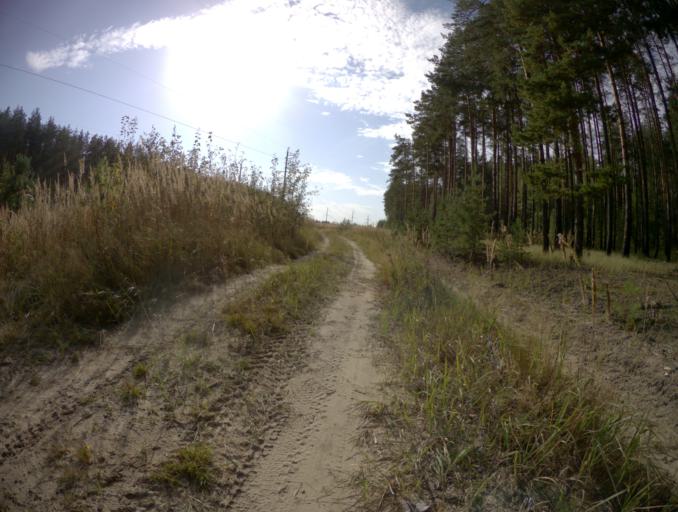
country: RU
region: Vladimir
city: Raduzhnyy
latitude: 56.0158
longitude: 40.2976
